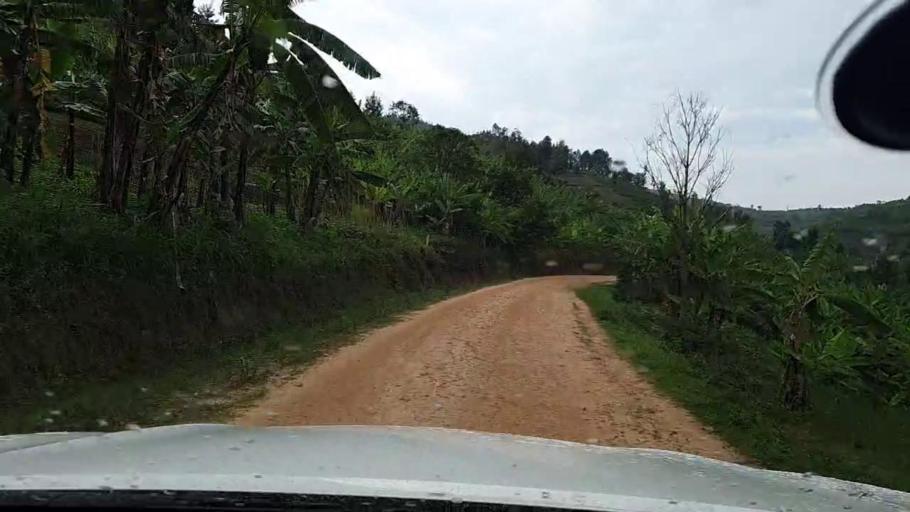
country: RW
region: Western Province
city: Kibuye
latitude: -2.1157
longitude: 29.4215
